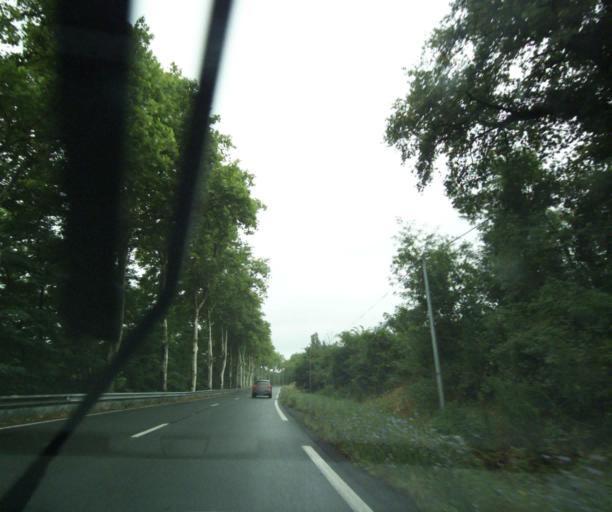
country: FR
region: Midi-Pyrenees
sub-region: Departement du Tarn
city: Le Garric
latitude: 43.9813
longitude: 2.1740
